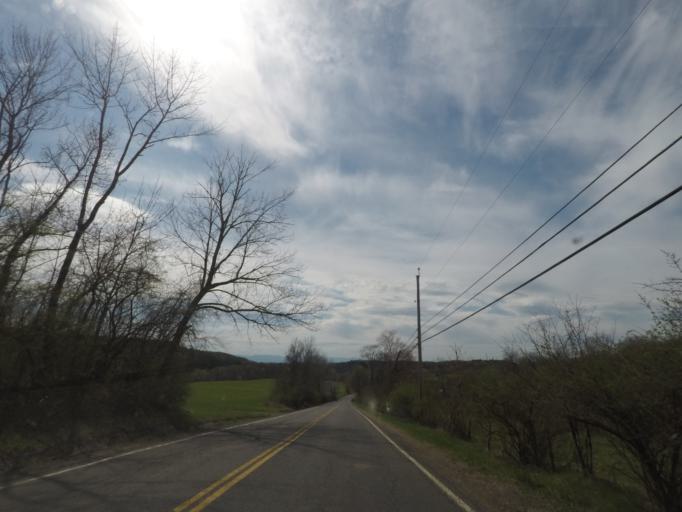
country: US
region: New York
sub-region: Columbia County
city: Chatham
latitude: 42.3562
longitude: -73.5429
